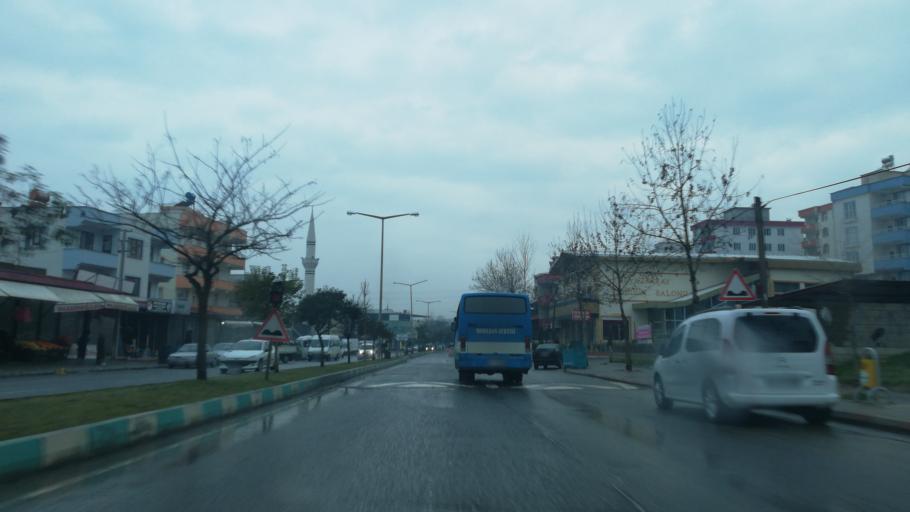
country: TR
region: Kahramanmaras
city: Kahramanmaras
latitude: 37.5818
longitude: 36.9636
